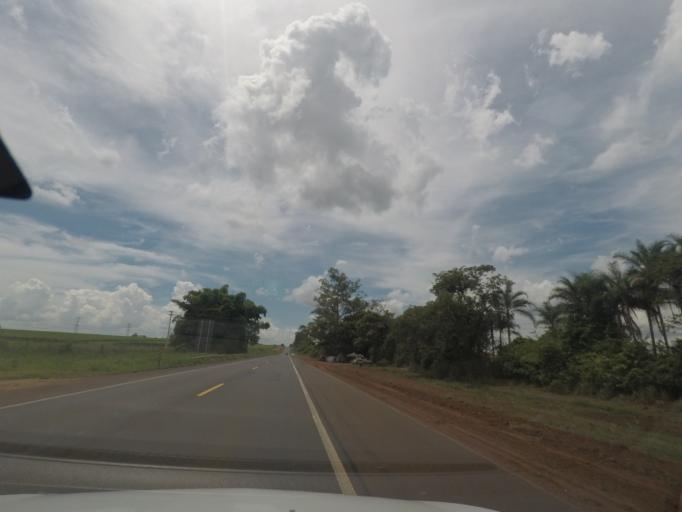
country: BR
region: Sao Paulo
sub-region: Barretos
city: Barretos
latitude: -20.3668
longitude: -48.6467
